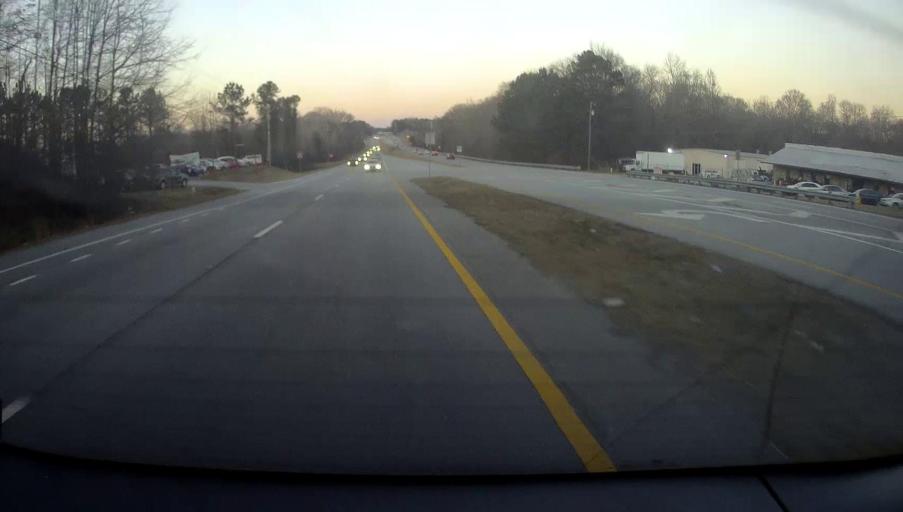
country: US
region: Georgia
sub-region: Fayette County
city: Fayetteville
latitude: 33.4913
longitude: -84.4317
